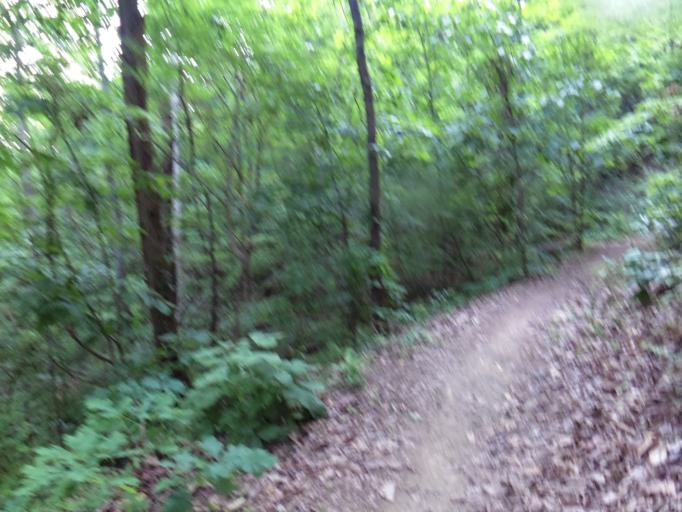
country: US
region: Tennessee
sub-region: Knox County
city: Knoxville
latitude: 36.0037
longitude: -83.9403
